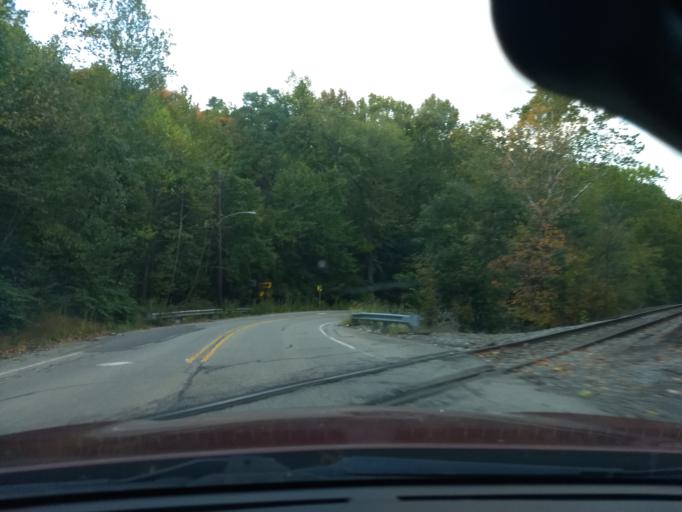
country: US
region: Pennsylvania
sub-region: Allegheny County
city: Brentwood
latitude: 40.3613
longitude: -79.9505
